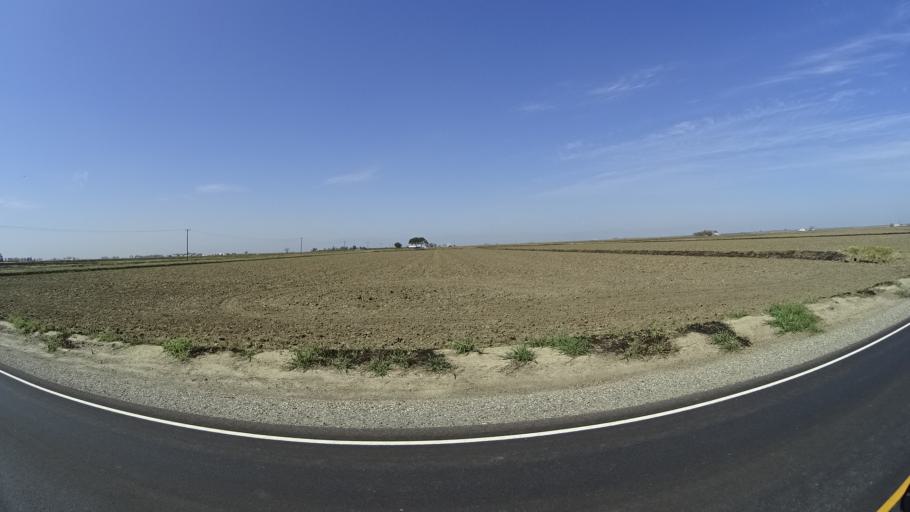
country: US
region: California
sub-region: Glenn County
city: Willows
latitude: 39.6023
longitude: -122.0658
